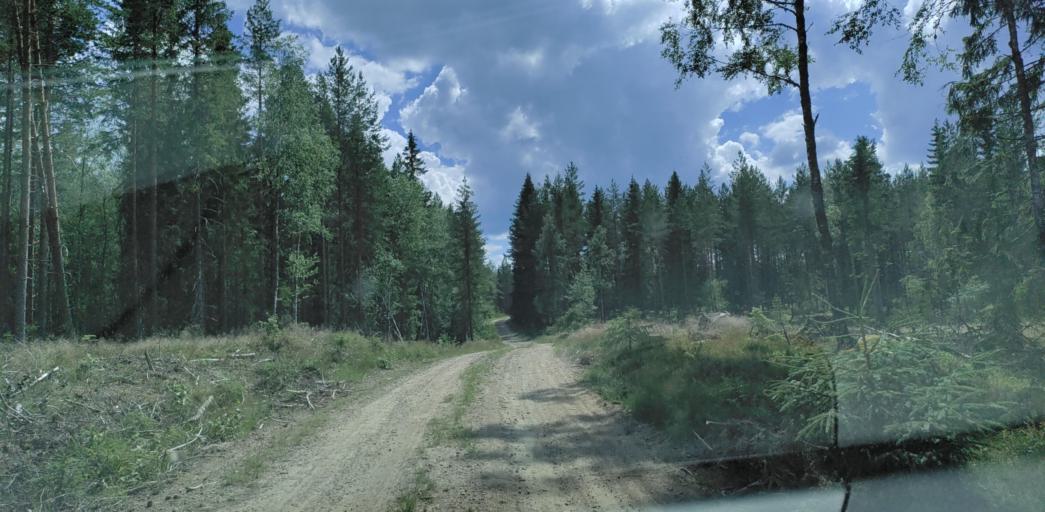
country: SE
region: Vaermland
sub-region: Hagfors Kommun
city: Ekshaerad
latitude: 60.0737
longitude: 13.3457
